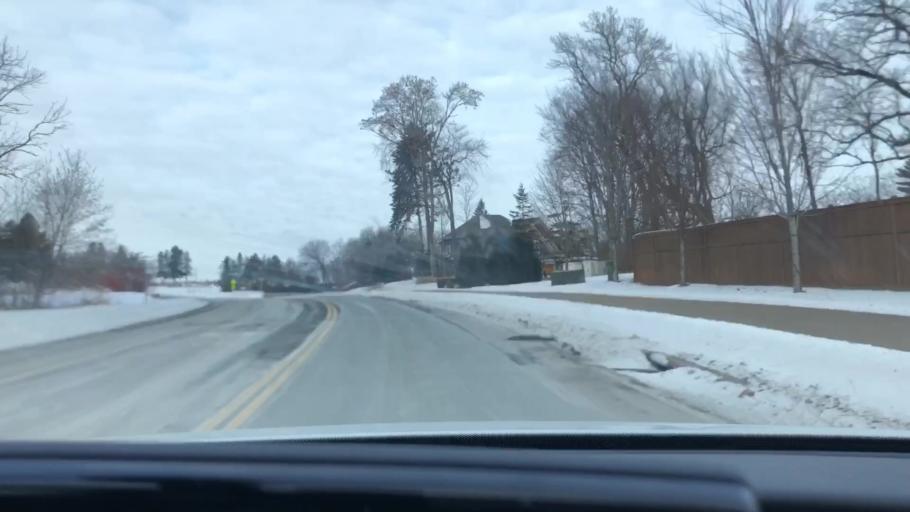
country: US
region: Minnesota
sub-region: Carver County
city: Waconia
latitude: 44.8497
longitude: -93.7735
